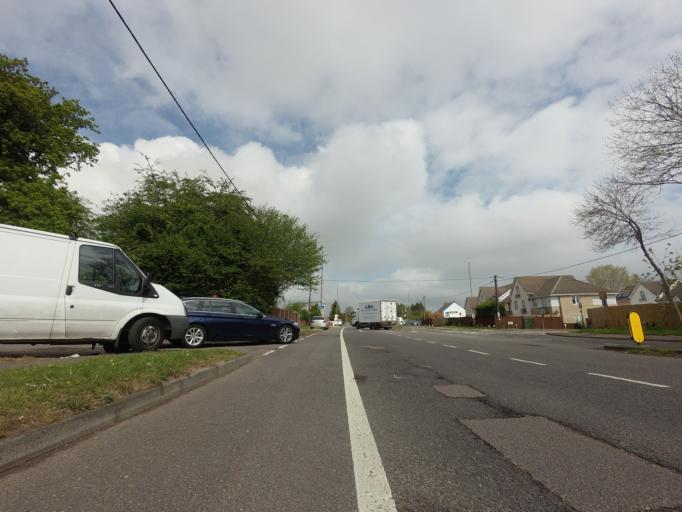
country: GB
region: England
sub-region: Kent
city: Eynsford
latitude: 51.3504
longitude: 0.2529
